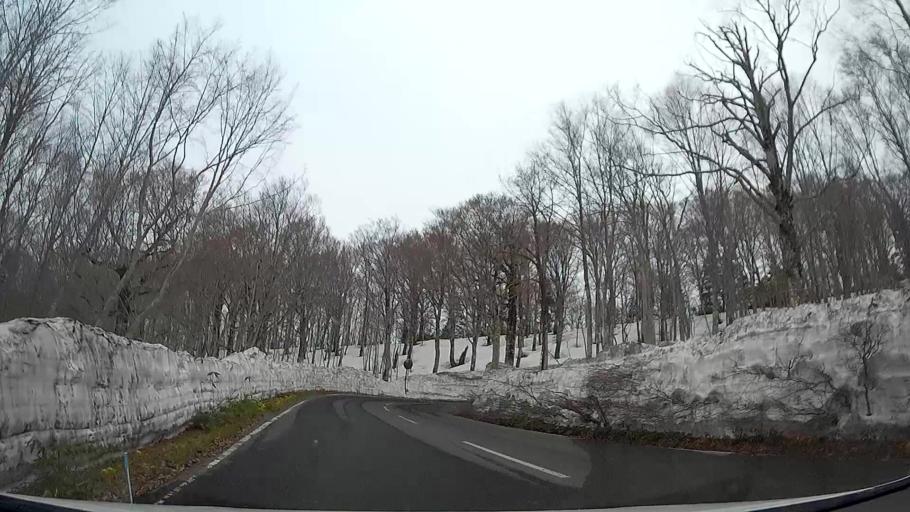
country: JP
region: Aomori
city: Aomori Shi
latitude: 40.6300
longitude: 140.9199
